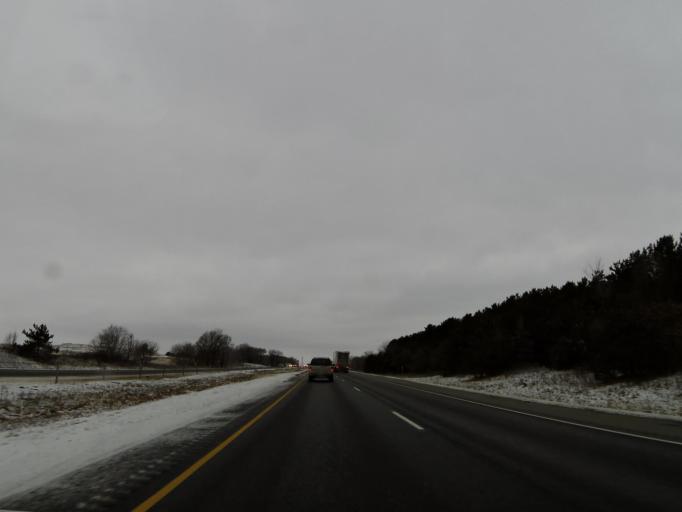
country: US
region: Wisconsin
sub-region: Eau Claire County
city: Eau Claire
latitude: 44.8543
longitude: -91.6507
